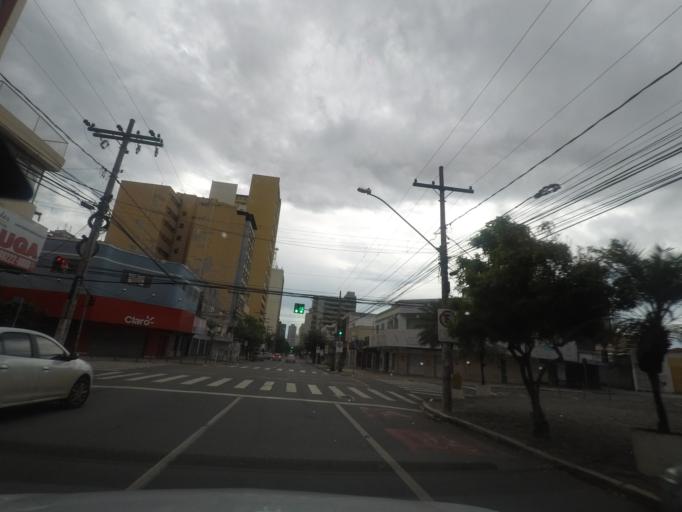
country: BR
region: Goias
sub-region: Goiania
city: Goiania
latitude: -16.6765
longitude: -49.2597
